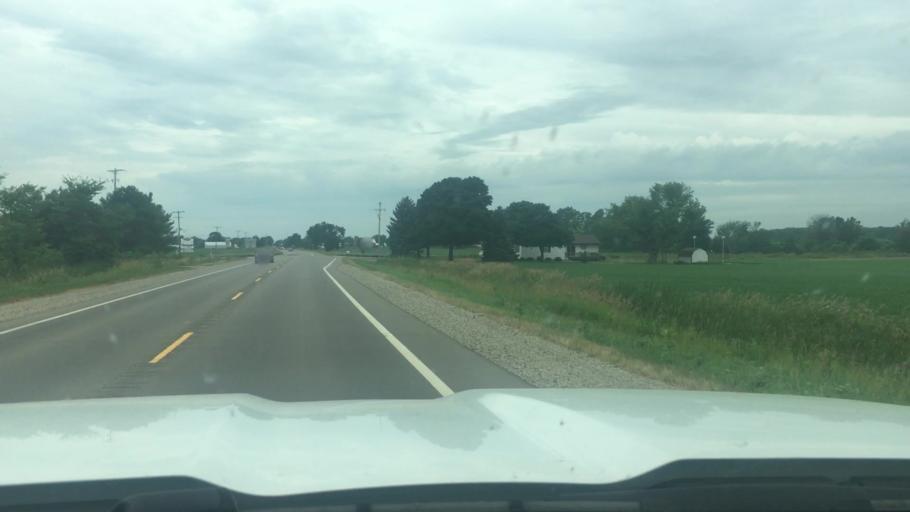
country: US
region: Michigan
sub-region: Clinton County
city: Fowler
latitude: 43.0018
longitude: -84.7177
